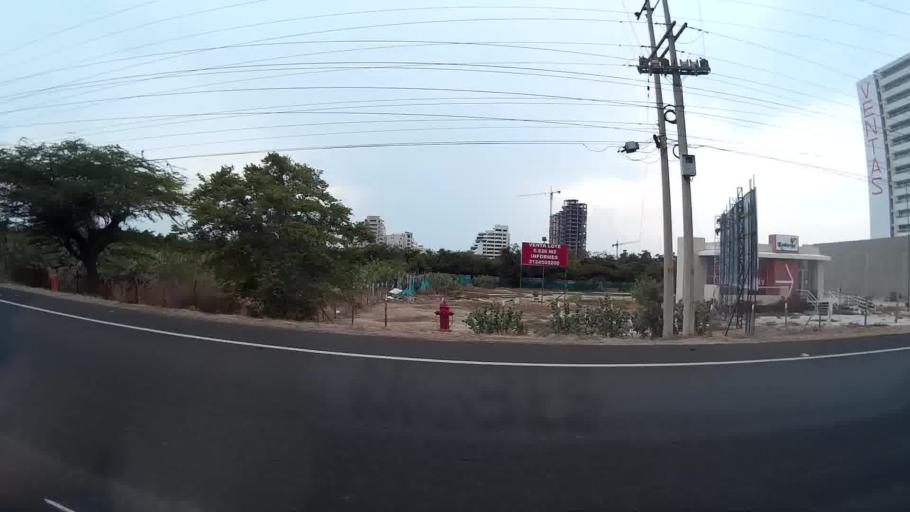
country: CO
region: Magdalena
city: Santa Marta
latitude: 11.1542
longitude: -74.2228
